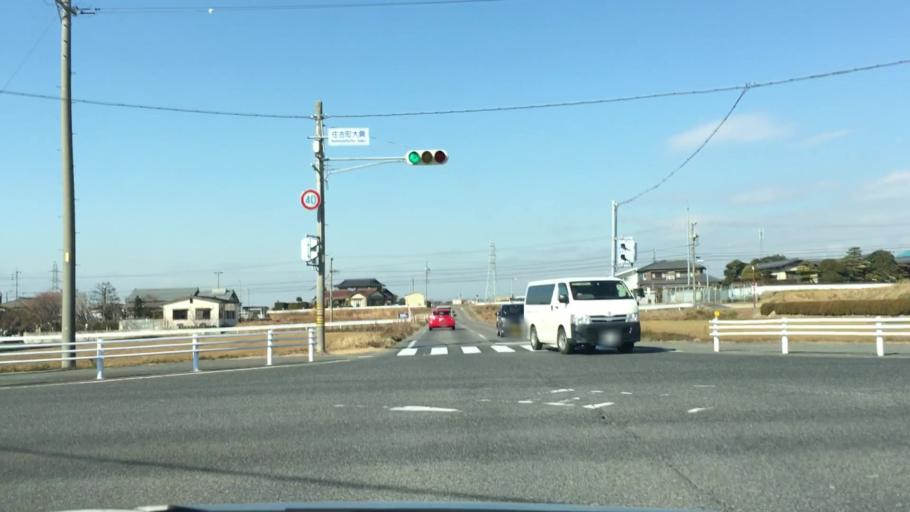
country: JP
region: Aichi
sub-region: Toyota-shi
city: Toyota
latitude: 35.0373
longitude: 137.1246
